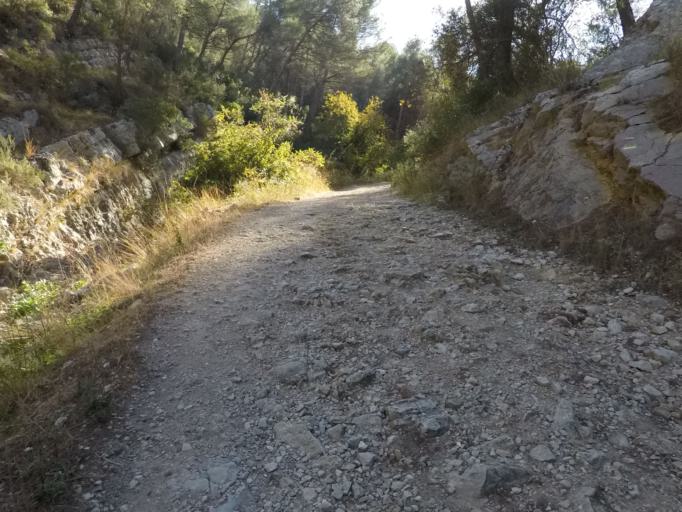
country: FR
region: Provence-Alpes-Cote d'Azur
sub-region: Departement des Bouches-du-Rhone
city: La Penne-sur-Huveaune
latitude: 43.2756
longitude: 5.4878
